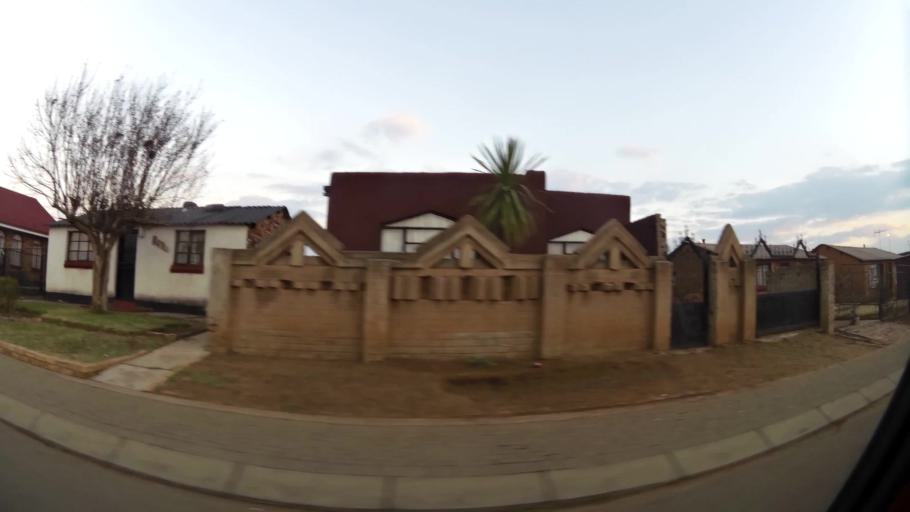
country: ZA
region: Gauteng
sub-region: City of Johannesburg Metropolitan Municipality
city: Orange Farm
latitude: -26.5560
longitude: 27.8754
